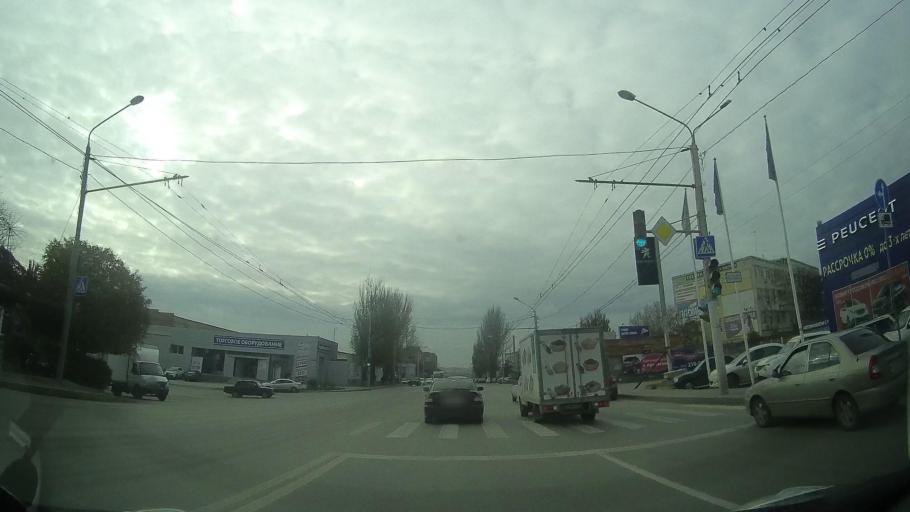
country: RU
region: Rostov
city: Severnyy
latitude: 47.2695
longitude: 39.6843
